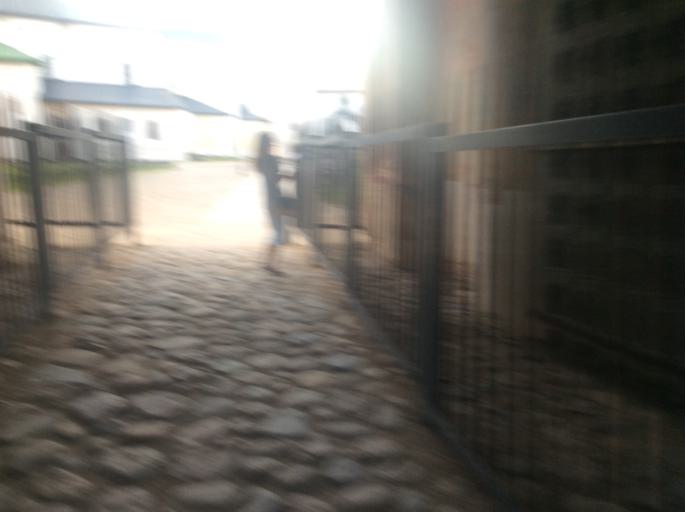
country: RU
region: Vologda
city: Kirillov
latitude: 59.8579
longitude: 38.3676
